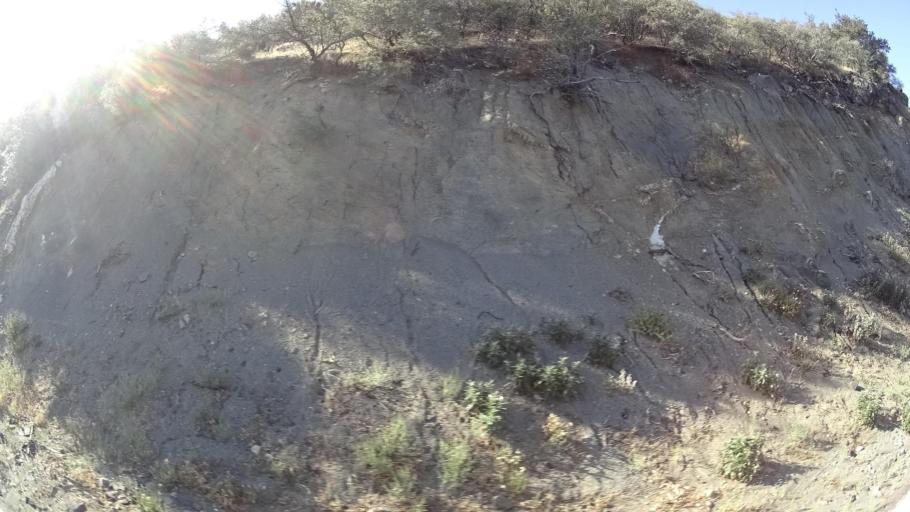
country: US
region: California
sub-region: San Diego County
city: Pine Valley
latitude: 32.8252
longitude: -116.4978
